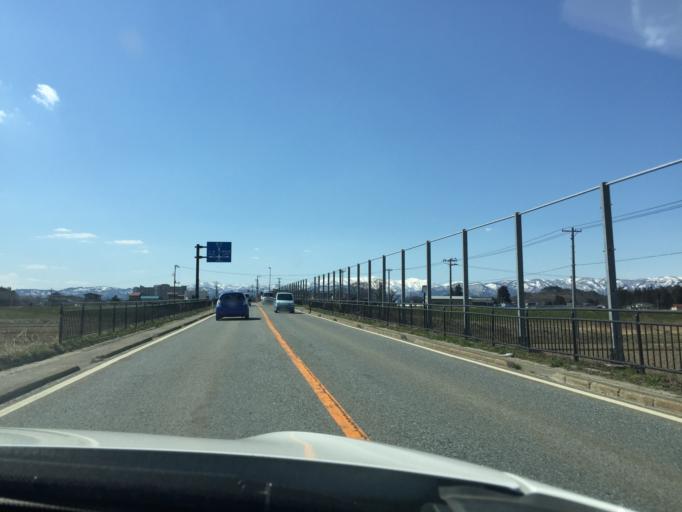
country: JP
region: Yamagata
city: Nagai
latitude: 38.0499
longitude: 140.0699
